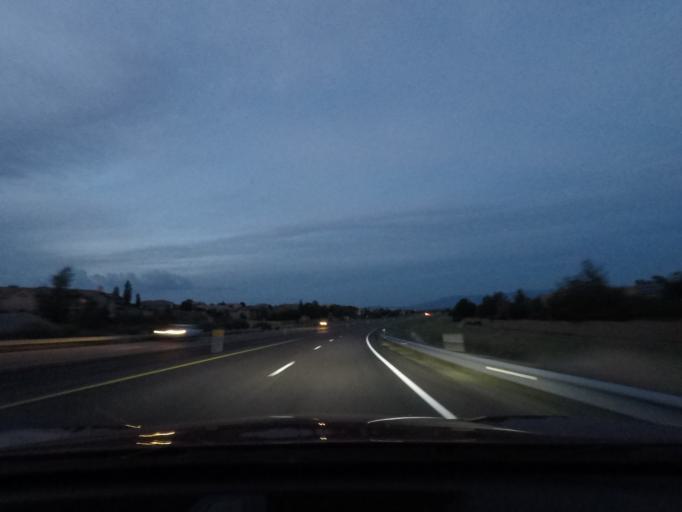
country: US
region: Arizona
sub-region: Yavapai County
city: Prescott
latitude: 34.6235
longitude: -112.4590
